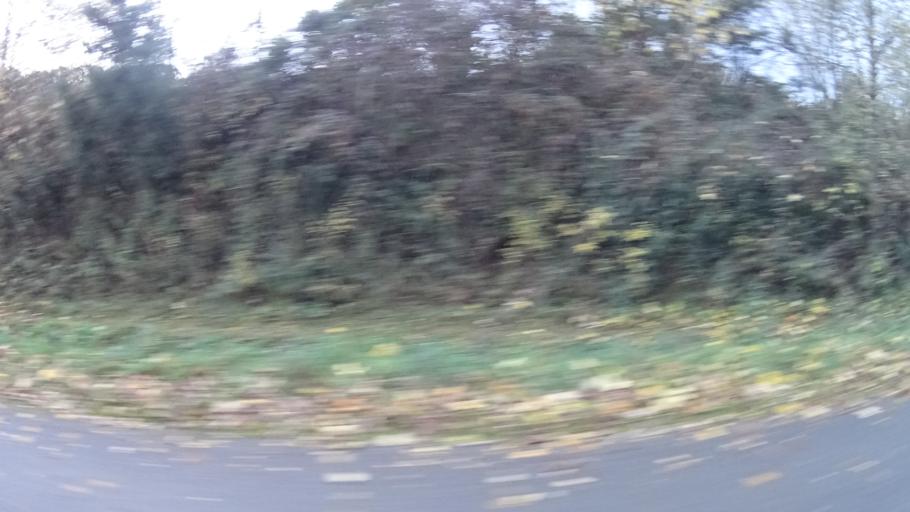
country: FR
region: Pays de la Loire
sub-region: Departement de la Loire-Atlantique
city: Saint-Nicolas-de-Redon
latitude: 47.6650
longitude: -2.0536
